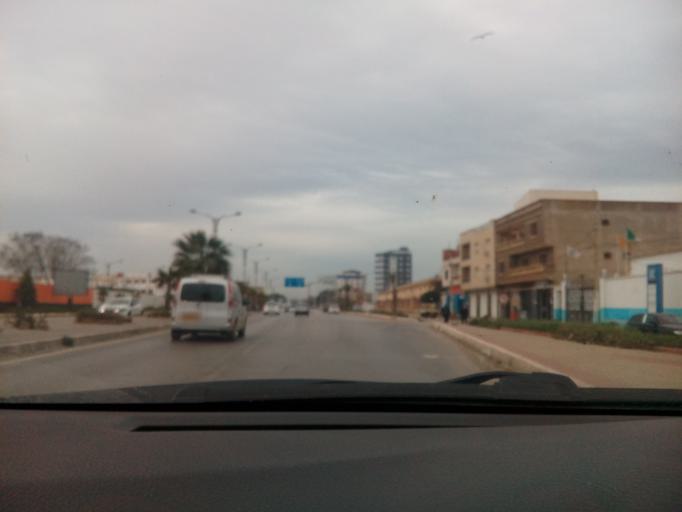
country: DZ
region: Oran
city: Oran
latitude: 35.6733
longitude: -0.6260
